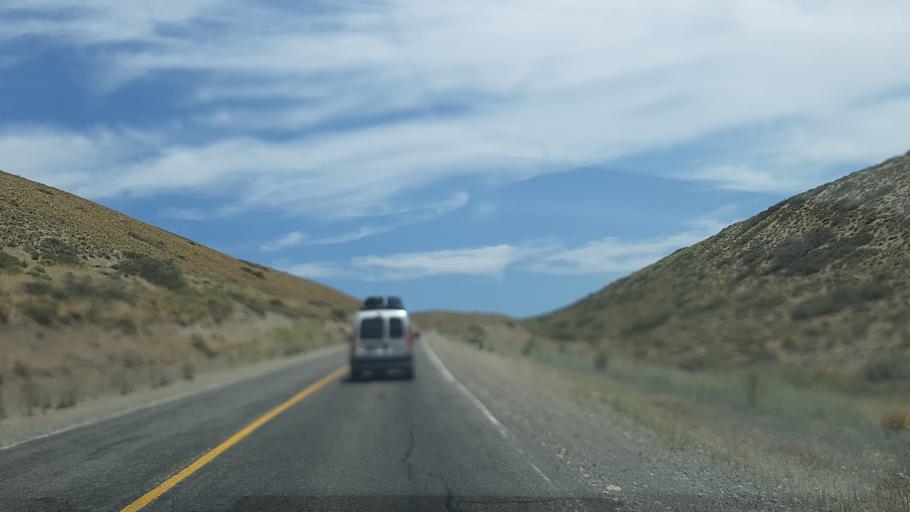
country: AR
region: Rio Negro
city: Pilcaniyeu
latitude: -40.4816
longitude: -70.6729
